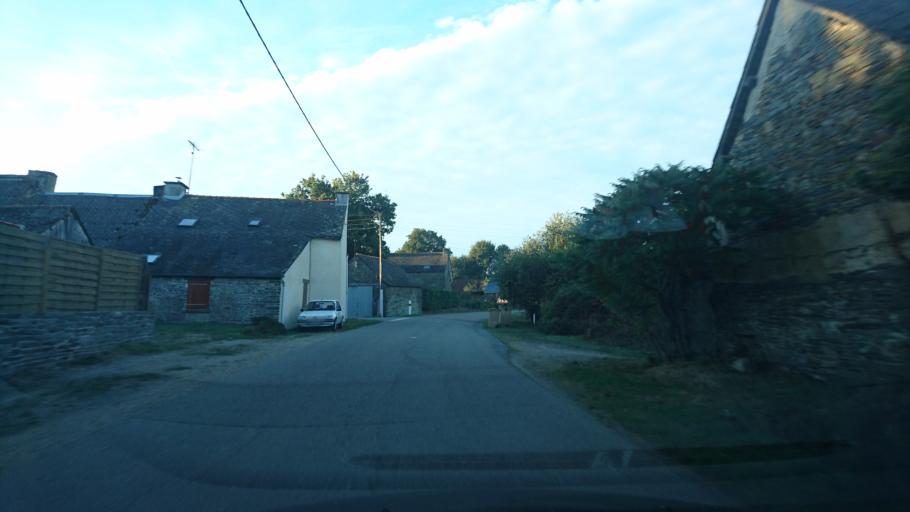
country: FR
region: Brittany
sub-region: Departement d'Ille-et-Vilaine
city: Sainte-Marie
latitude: 47.7045
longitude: -1.9935
